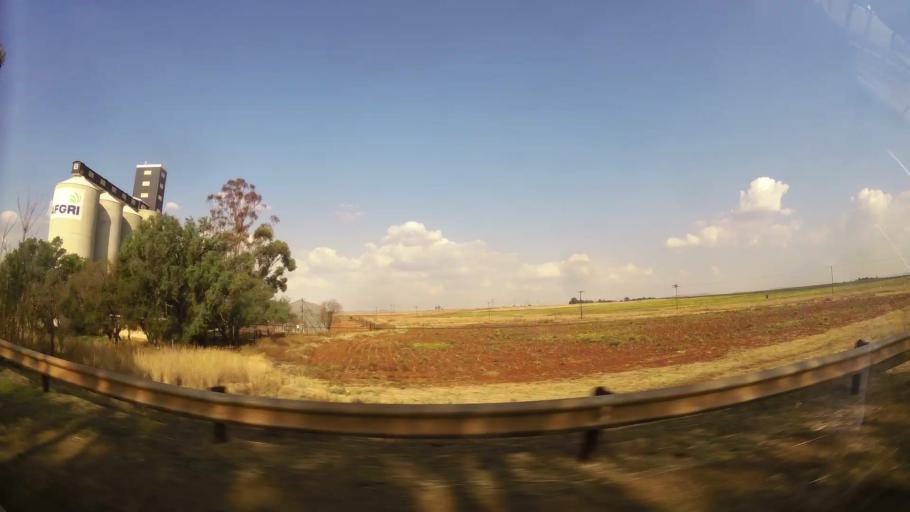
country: ZA
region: Gauteng
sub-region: Sedibeng District Municipality
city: Heidelberg
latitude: -26.3852
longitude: 28.3065
